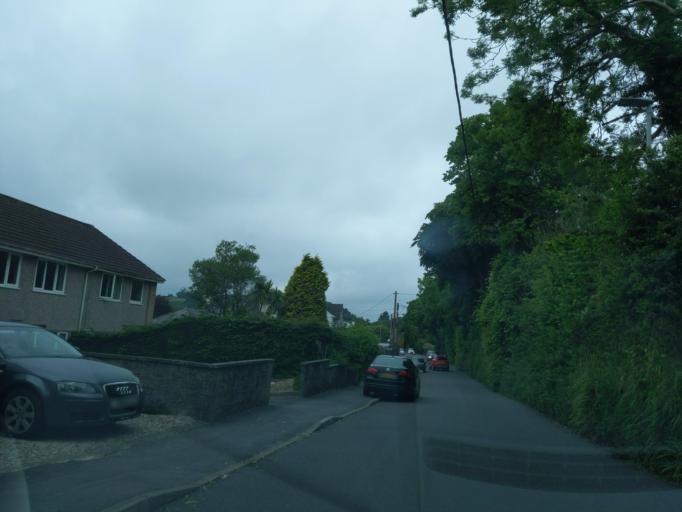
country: GB
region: England
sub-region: Devon
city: Plympton
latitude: 50.3839
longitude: -4.0432
